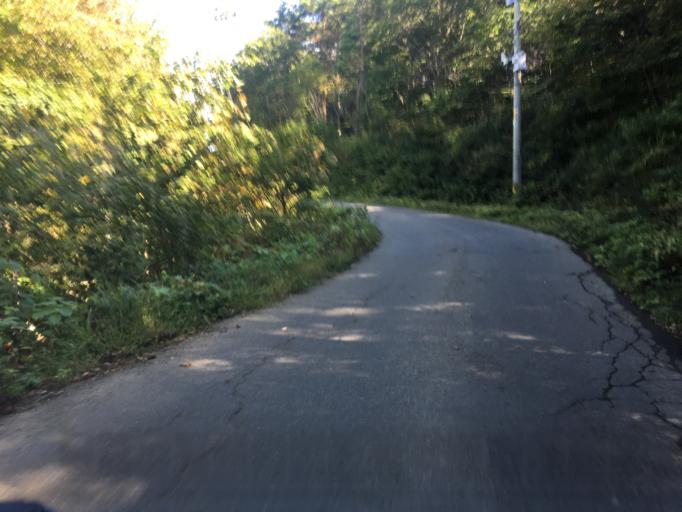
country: JP
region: Yamagata
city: Yonezawa
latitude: 37.8064
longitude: 140.2786
